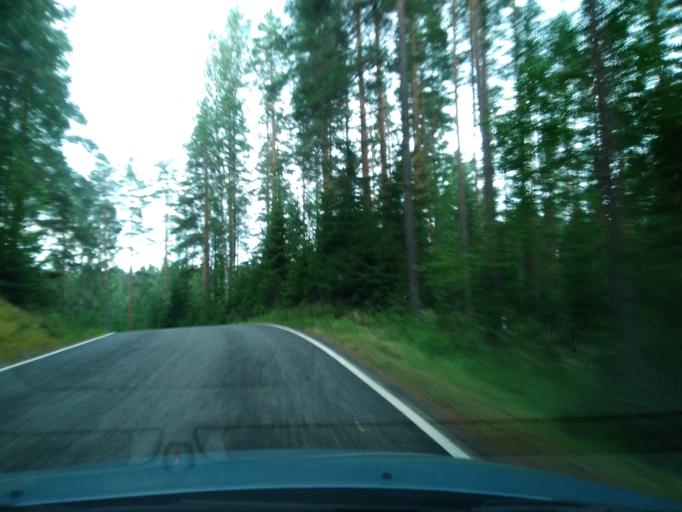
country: FI
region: Uusimaa
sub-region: Helsinki
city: Kaerkoelae
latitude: 60.7872
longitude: 24.0799
